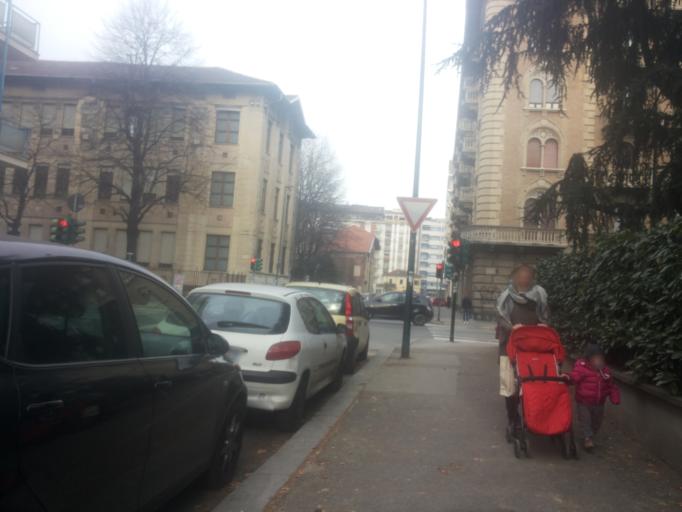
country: IT
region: Piedmont
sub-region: Provincia di Torino
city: Lesna
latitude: 45.0601
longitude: 7.6480
